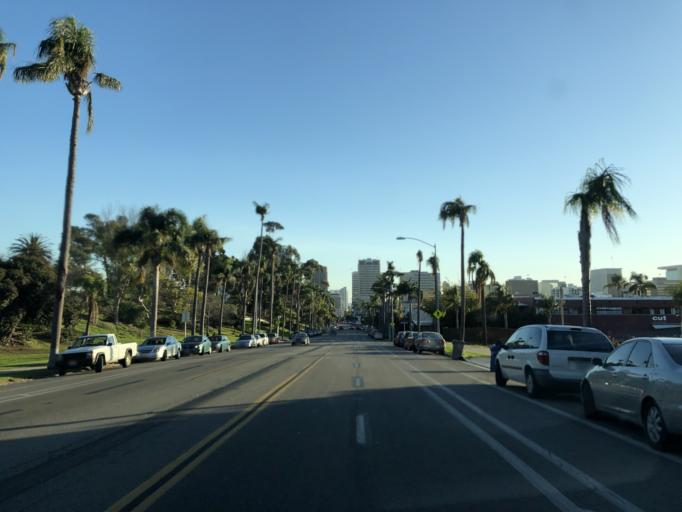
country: US
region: California
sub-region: San Diego County
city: San Diego
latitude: 32.7271
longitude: -117.1595
